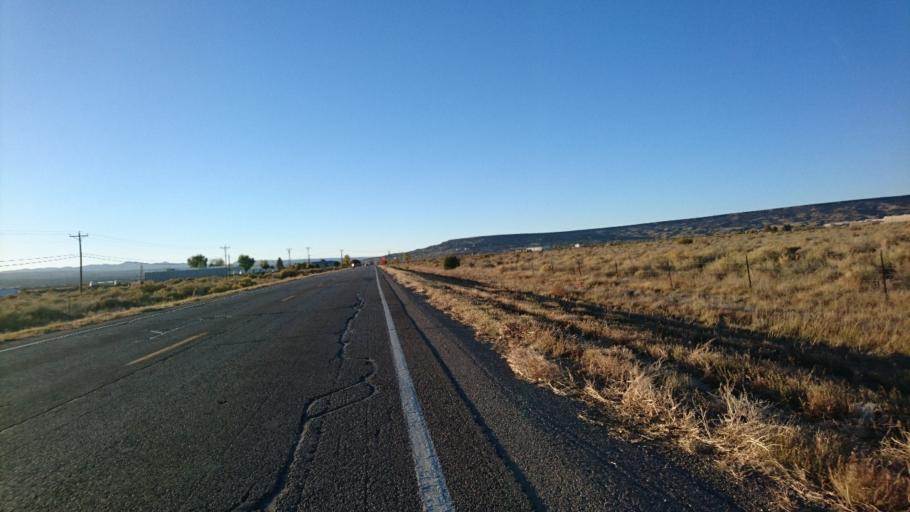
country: US
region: New Mexico
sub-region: Cibola County
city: Grants
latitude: 35.1329
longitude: -107.8150
